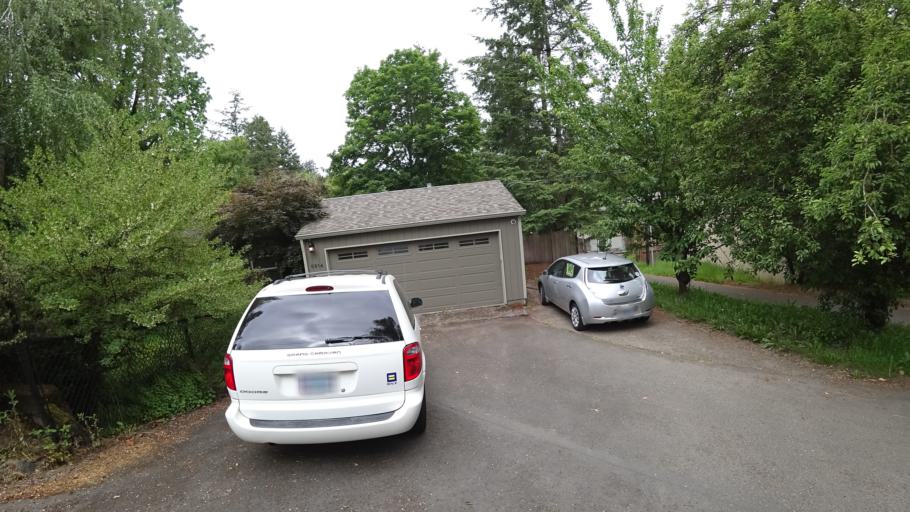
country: US
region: Oregon
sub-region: Washington County
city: Garden Home-Whitford
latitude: 45.4669
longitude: -122.7370
